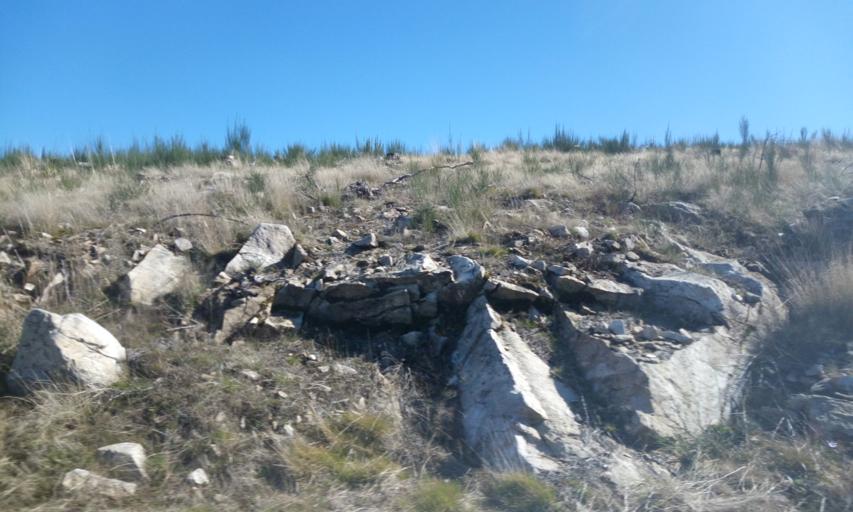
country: PT
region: Guarda
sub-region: Manteigas
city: Manteigas
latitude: 40.4955
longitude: -7.5260
